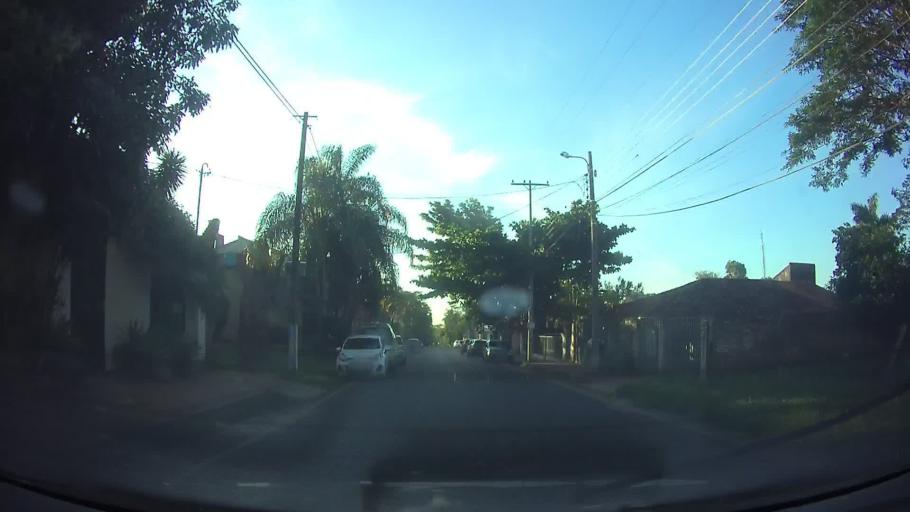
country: PY
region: Central
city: Fernando de la Mora
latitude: -25.2651
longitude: -57.5096
